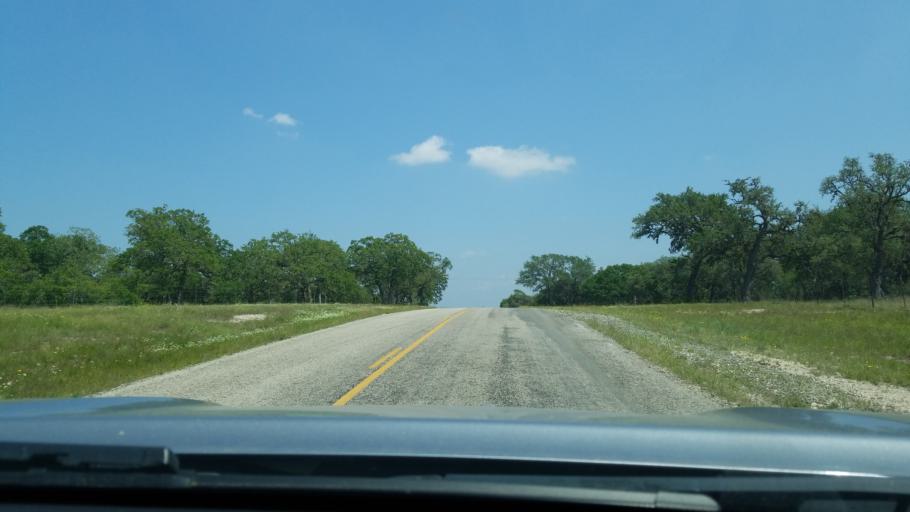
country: US
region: Texas
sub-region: Blanco County
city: Blanco
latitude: 29.9742
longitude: -98.5350
